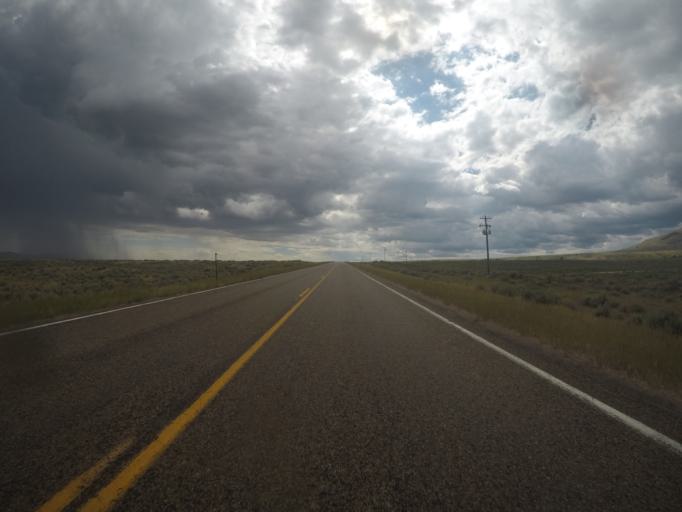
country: US
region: Utah
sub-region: Daggett County
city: Manila
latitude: 41.0225
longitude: -109.9033
